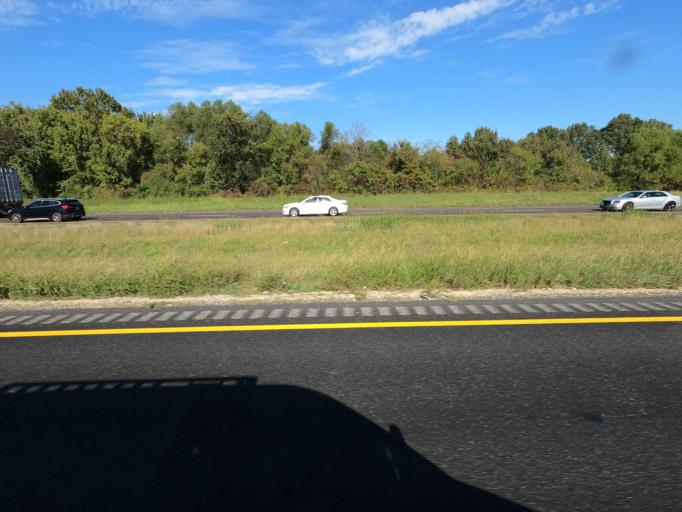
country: US
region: Tennessee
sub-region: Tipton County
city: Mason
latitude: 35.3384
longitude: -89.5411
